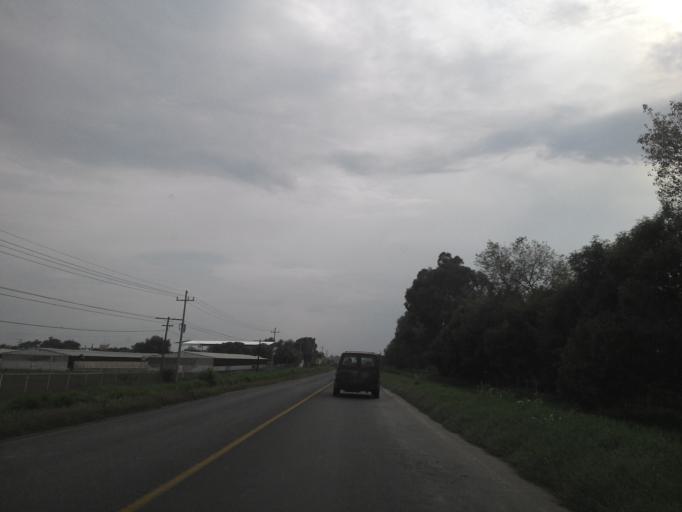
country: MX
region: Jalisco
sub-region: Acatic
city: Tierras Coloradas
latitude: 20.7560
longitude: -102.8264
